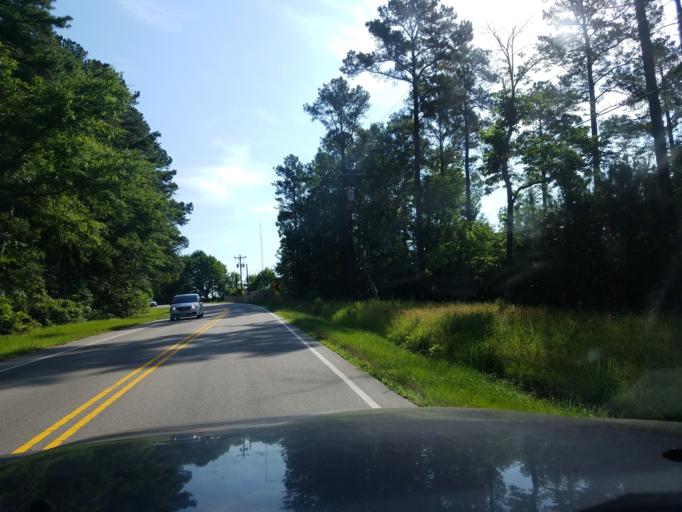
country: US
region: North Carolina
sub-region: Granville County
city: Butner
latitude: 36.1608
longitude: -78.7626
